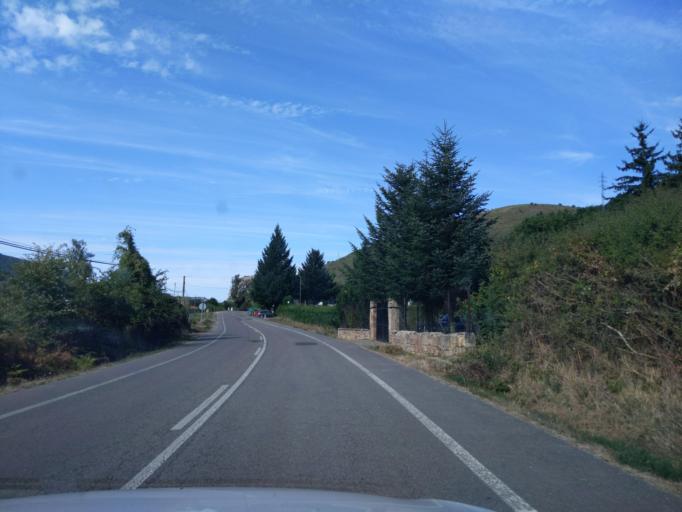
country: ES
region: La Rioja
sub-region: Provincia de La Rioja
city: Ezcaray
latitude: 42.3121
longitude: -3.0159
